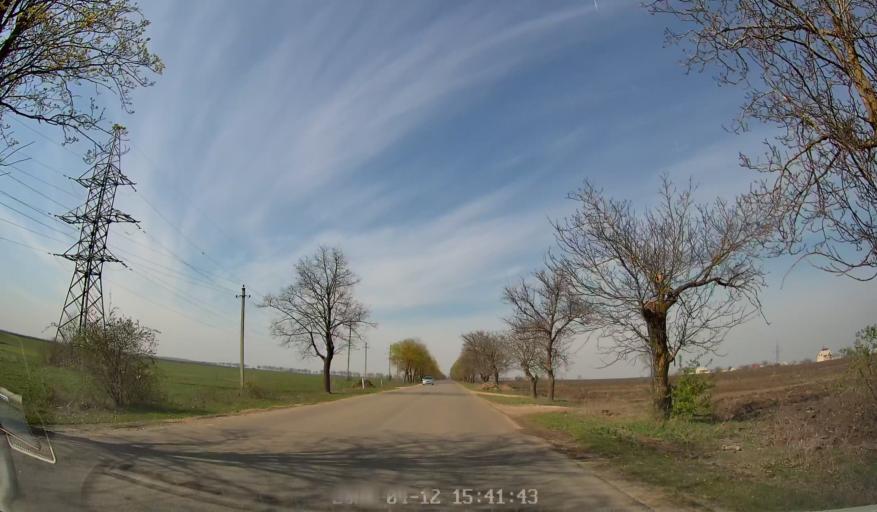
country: MD
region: Telenesti
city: Cocieri
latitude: 47.3130
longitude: 29.0568
